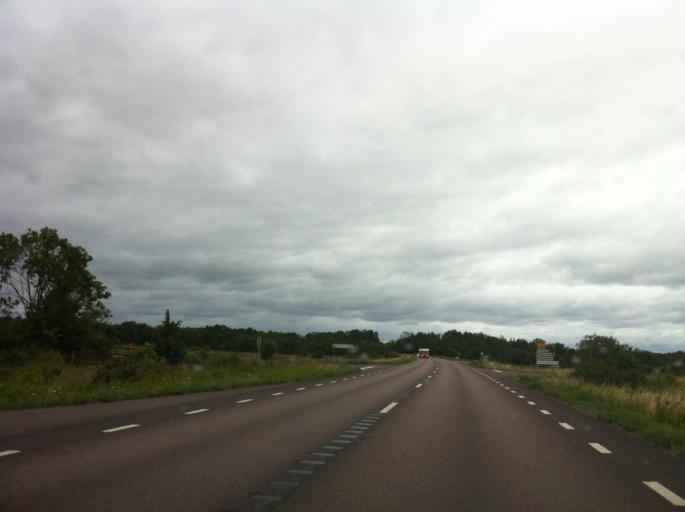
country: SE
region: Kalmar
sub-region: Borgholms Kommun
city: Borgholm
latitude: 57.0794
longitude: 16.9169
